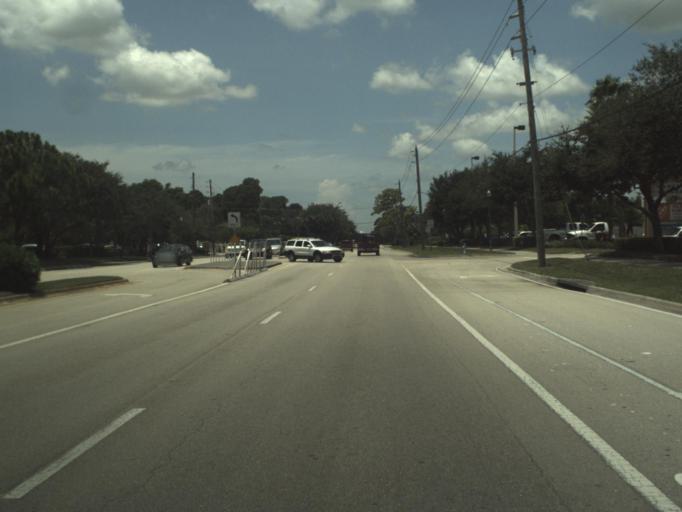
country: US
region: Florida
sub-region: Martin County
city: Port Salerno
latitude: 27.1654
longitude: -80.2286
